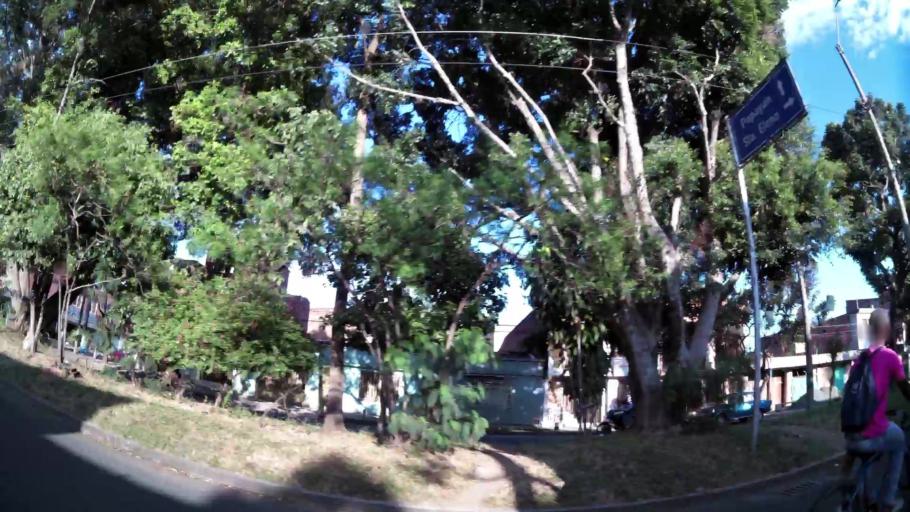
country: CO
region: Valle del Cauca
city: Cali
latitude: 3.4298
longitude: -76.5167
